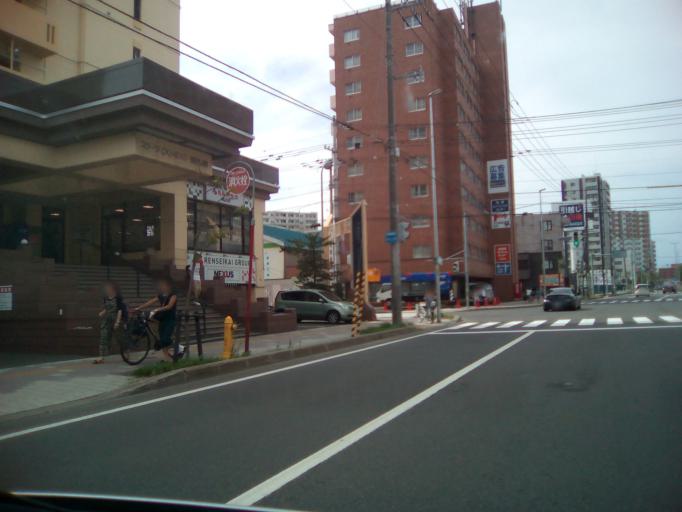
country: JP
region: Hokkaido
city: Sapporo
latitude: 43.0521
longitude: 141.3843
